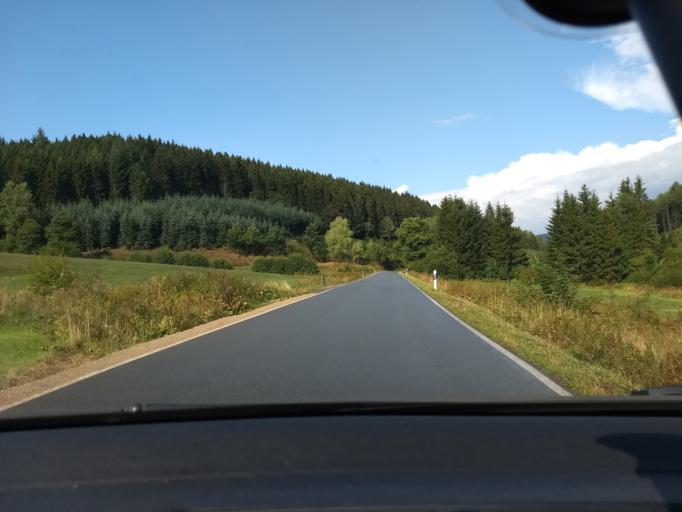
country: DE
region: North Rhine-Westphalia
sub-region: Regierungsbezirk Arnsberg
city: Finnentrop
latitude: 51.2306
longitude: 8.0525
